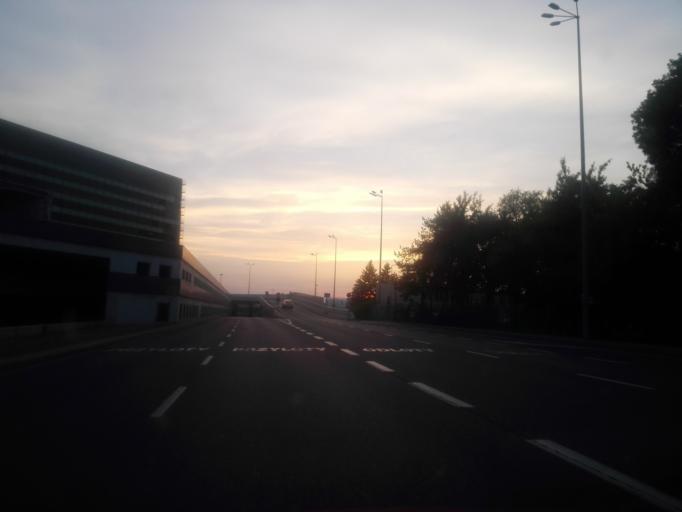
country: PL
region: Masovian Voivodeship
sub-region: Warszawa
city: Wlochy
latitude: 52.1724
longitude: 20.9754
